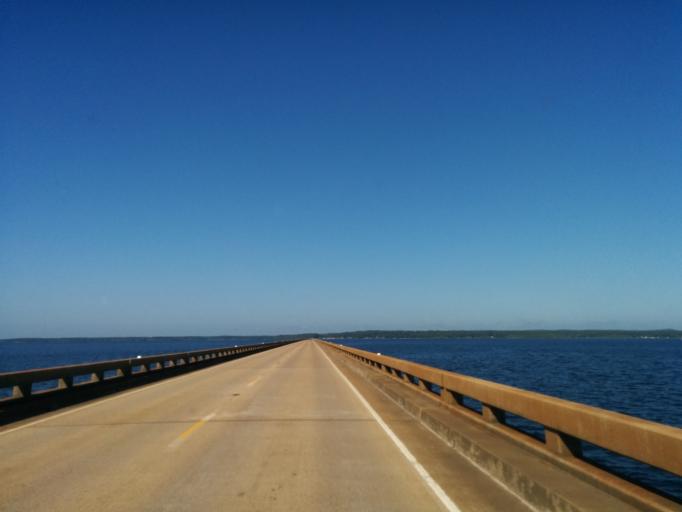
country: US
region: Texas
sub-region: Sabine County
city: Milam
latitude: 31.4837
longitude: -93.7173
